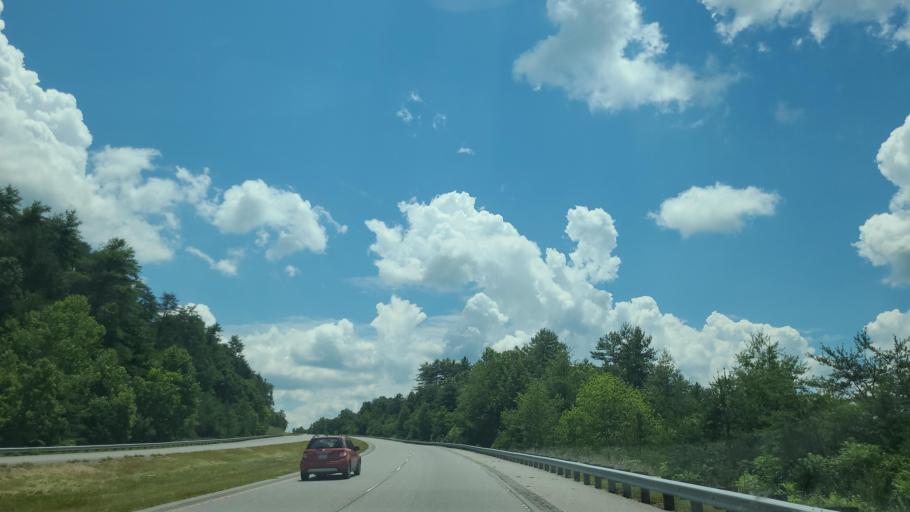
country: US
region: North Carolina
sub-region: Madison County
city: Marshall
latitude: 35.7586
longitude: -82.6167
